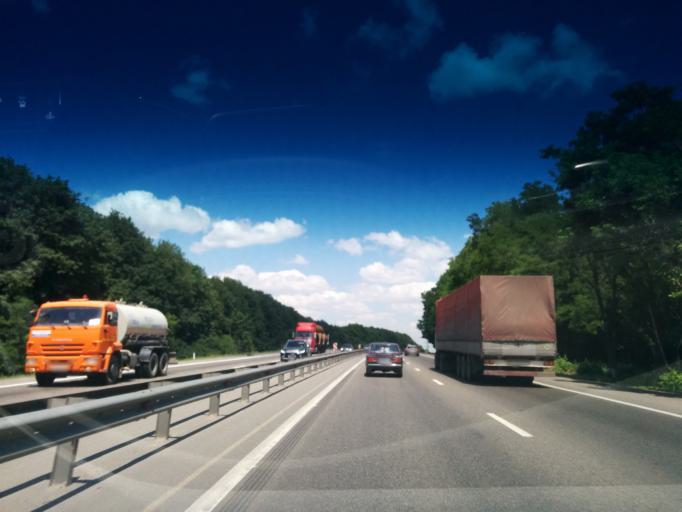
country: RU
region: Rostov
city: Aksay
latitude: 47.3228
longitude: 39.8630
